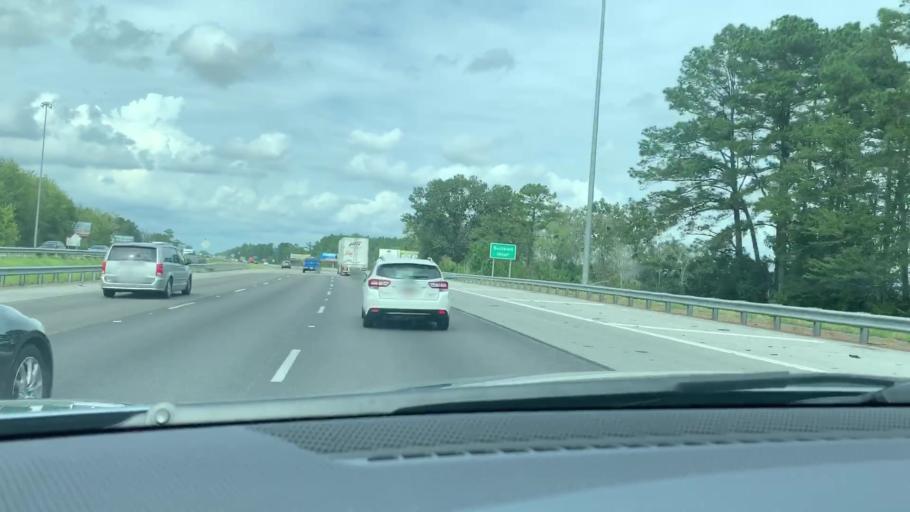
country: US
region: Georgia
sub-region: Liberty County
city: Midway
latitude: 31.6580
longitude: -81.3925
